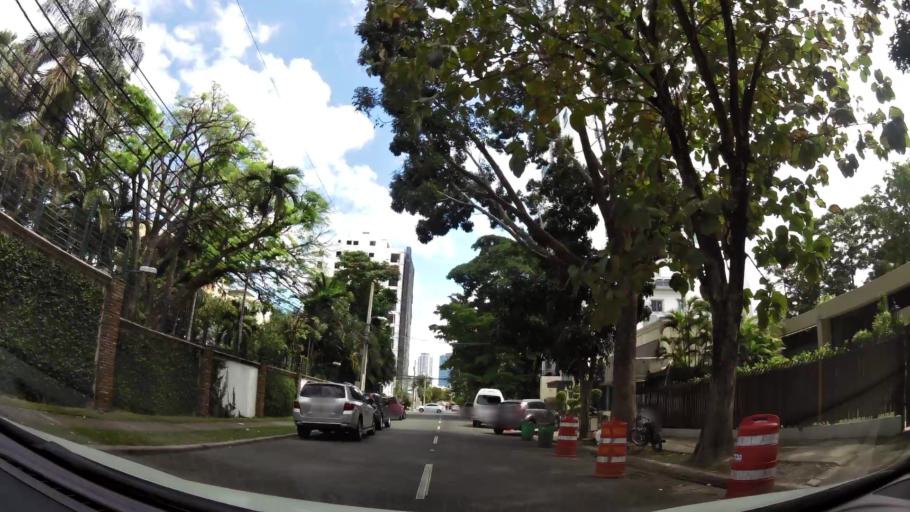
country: DO
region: Nacional
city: La Julia
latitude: 18.4706
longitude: -69.9364
